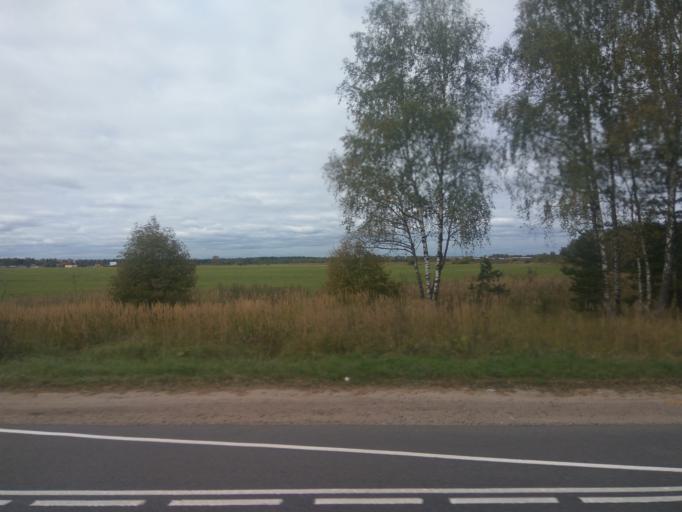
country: RU
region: Moskovskaya
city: Krasnoarmeysk
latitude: 56.0137
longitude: 38.1547
